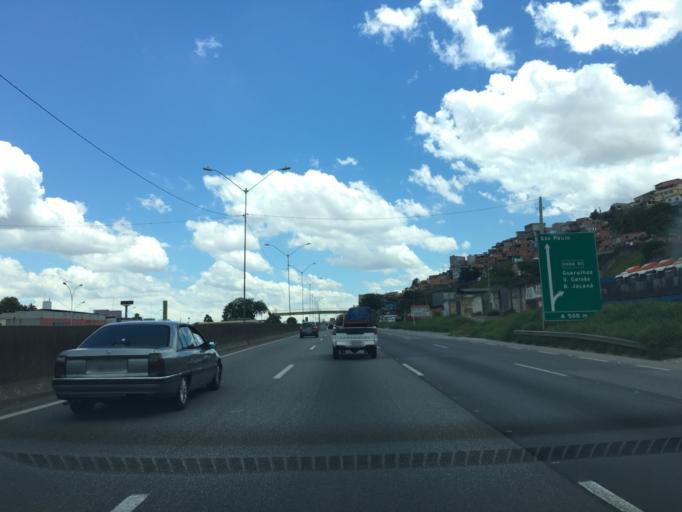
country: BR
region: Sao Paulo
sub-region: Guarulhos
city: Guarulhos
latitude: -23.4464
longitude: -46.5691
